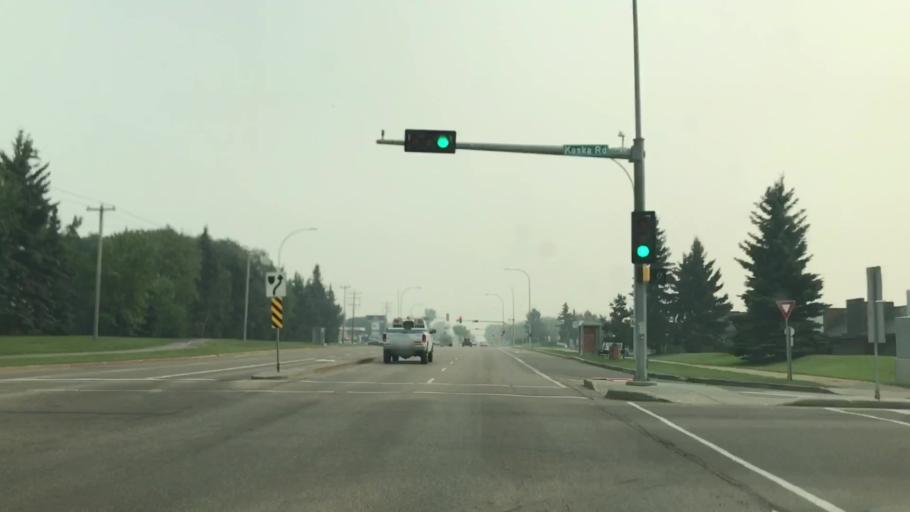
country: CA
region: Alberta
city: Sherwood Park
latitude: 53.5396
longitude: -113.3202
